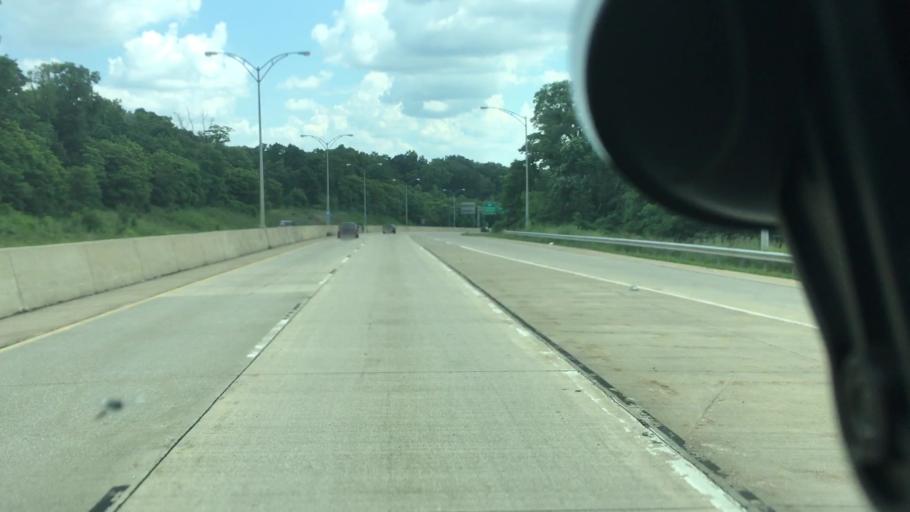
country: US
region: Ohio
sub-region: Trumbull County
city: Churchill
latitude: 41.1300
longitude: -80.6750
